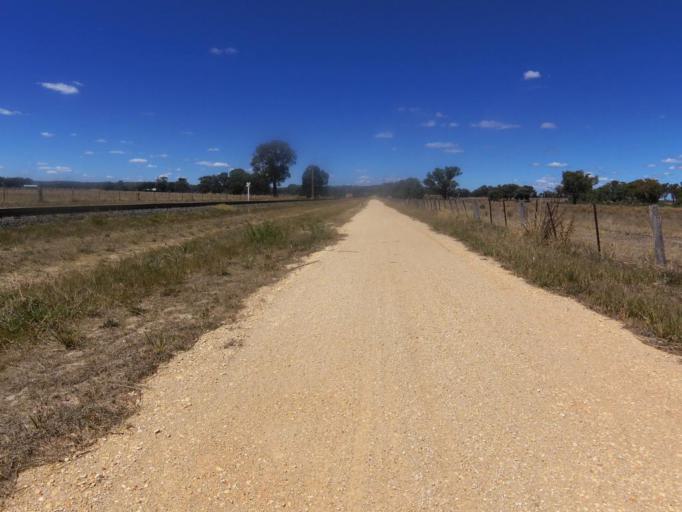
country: AU
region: Victoria
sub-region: Mount Alexander
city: Castlemaine
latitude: -37.0189
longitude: 144.1454
